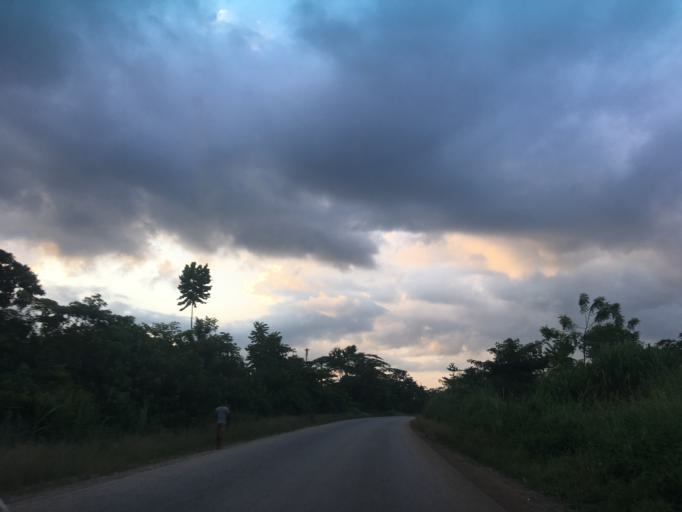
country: GH
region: Western
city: Bibiani
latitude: 6.7408
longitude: -2.5032
